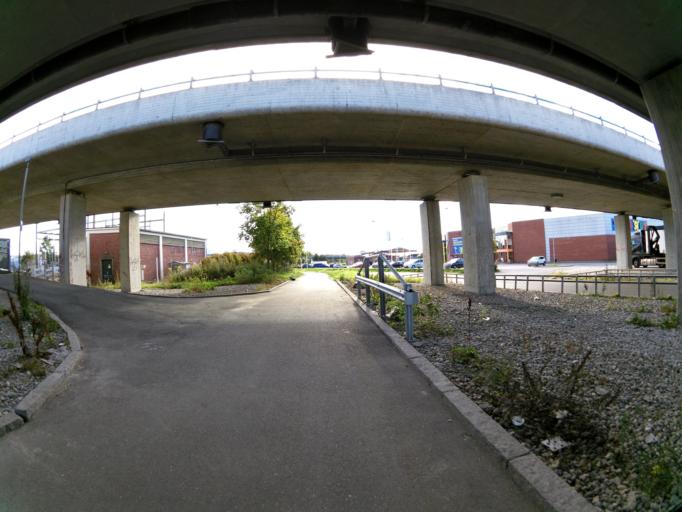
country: NO
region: Ostfold
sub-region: Sarpsborg
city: Sarpsborg
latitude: 59.2755
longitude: 11.0880
